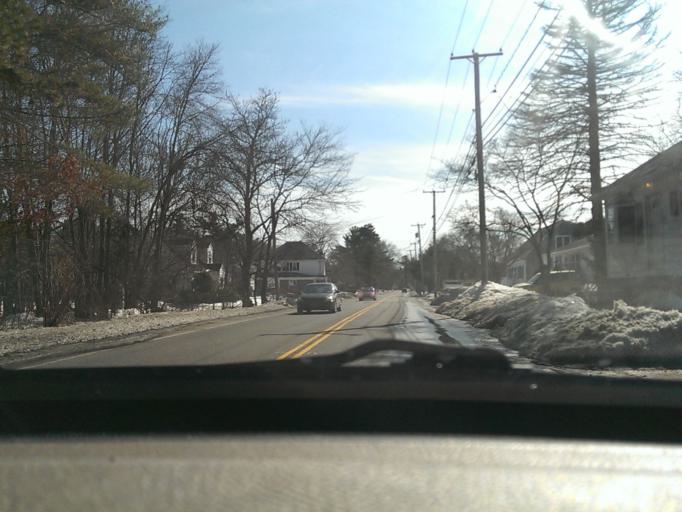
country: US
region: Massachusetts
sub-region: Bristol County
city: Head of Westport
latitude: 41.6513
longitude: -71.0382
